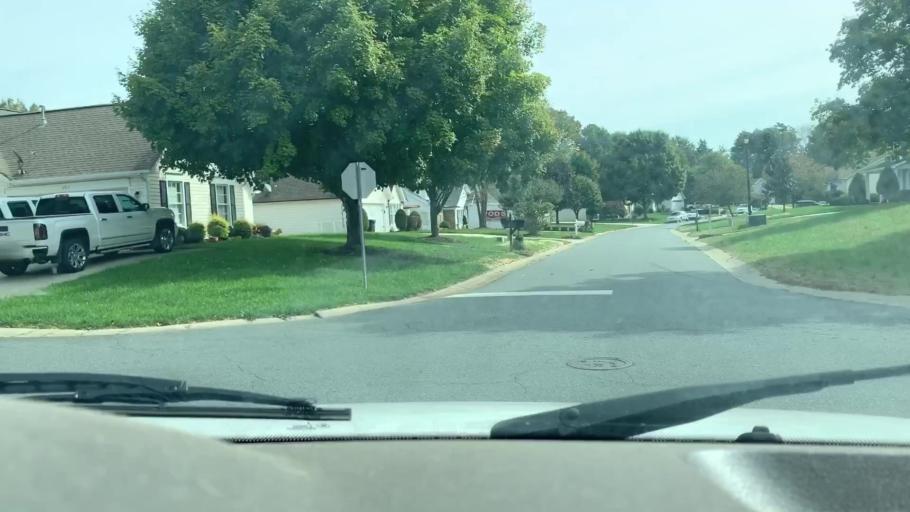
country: US
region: North Carolina
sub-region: Mecklenburg County
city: Huntersville
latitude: 35.4137
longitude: -80.8273
